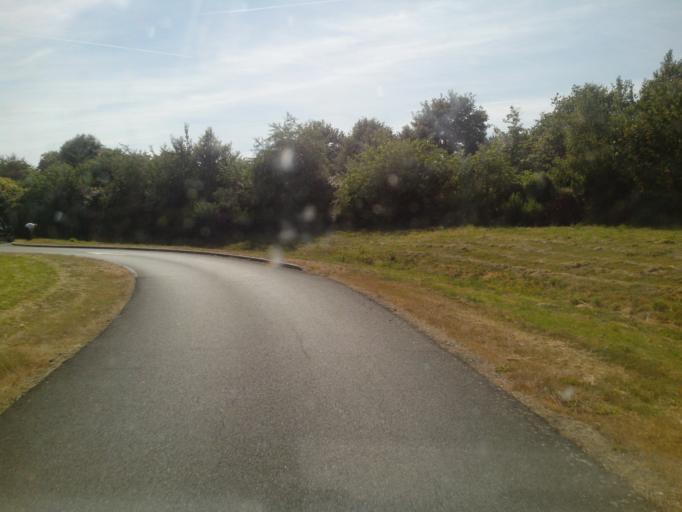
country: FR
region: Pays de la Loire
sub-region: Departement de la Loire-Atlantique
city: Nozay
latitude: 47.5367
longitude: -1.6381
